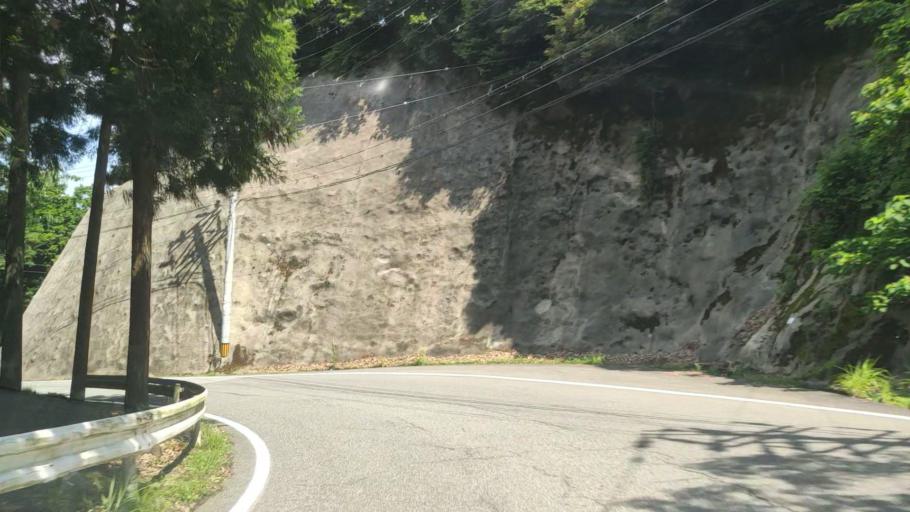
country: JP
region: Hyogo
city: Toyooka
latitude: 35.6404
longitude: 134.7665
